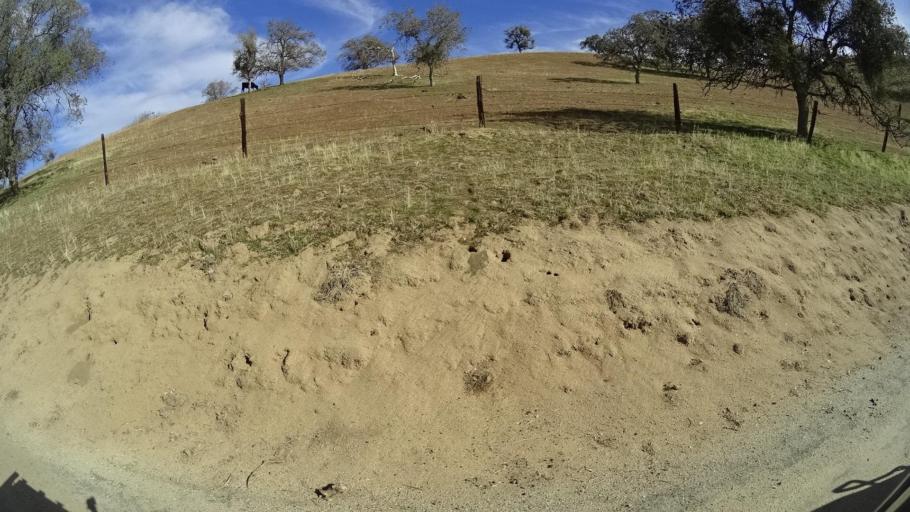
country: US
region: California
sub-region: Kern County
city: Oildale
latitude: 35.5680
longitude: -118.7996
